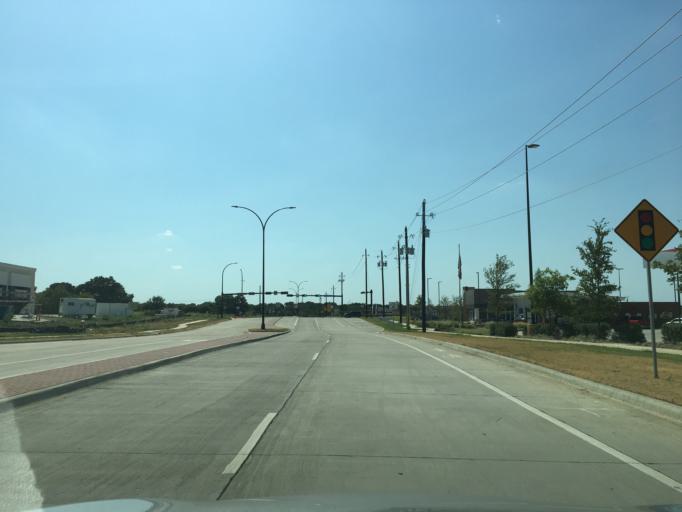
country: US
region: Texas
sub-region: Tarrant County
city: Kennedale
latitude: 32.6463
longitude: -97.1875
